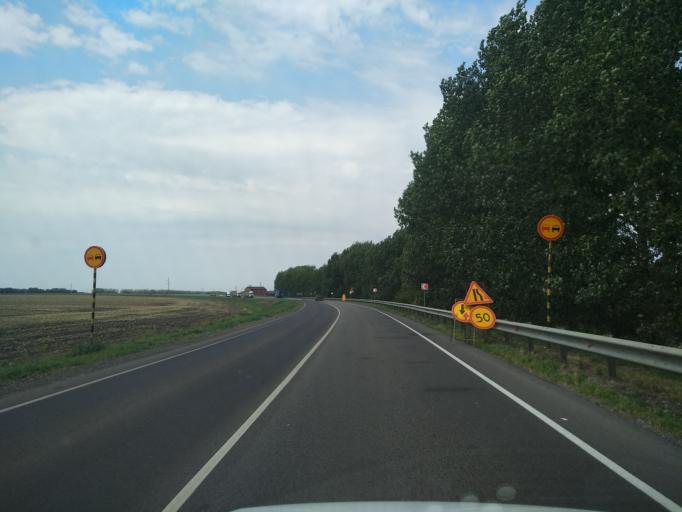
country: RU
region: Voronezj
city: Pereleshino
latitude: 51.8030
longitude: 40.1616
